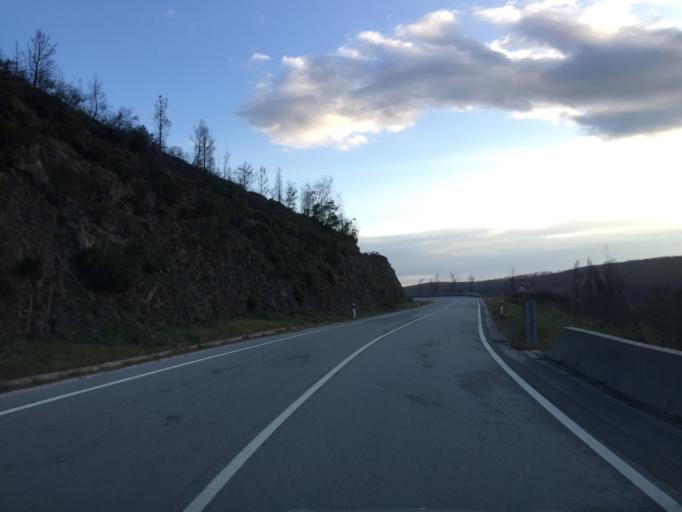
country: PT
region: Coimbra
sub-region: Pampilhosa da Serra
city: Pampilhosa da Serra
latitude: 40.0966
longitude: -7.9876
